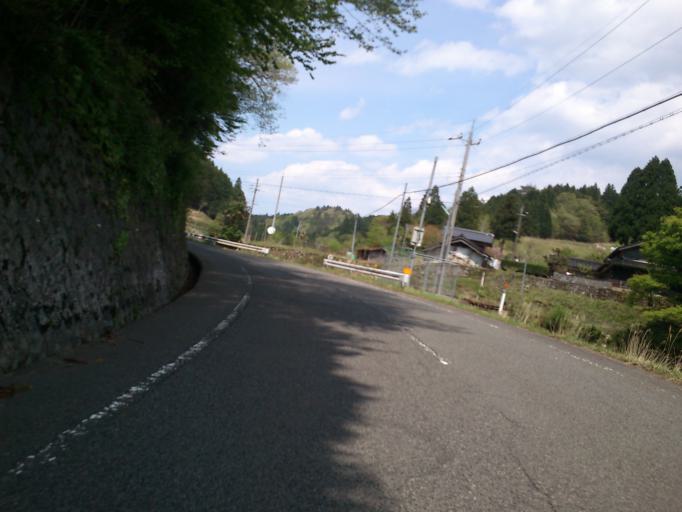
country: JP
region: Hyogo
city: Toyooka
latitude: 35.3991
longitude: 134.9464
